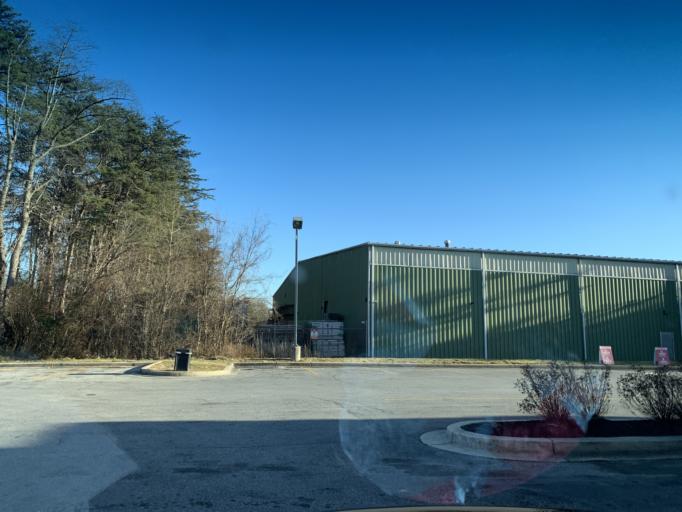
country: US
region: Maryland
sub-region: Anne Arundel County
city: Jessup
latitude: 39.1831
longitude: -76.7636
